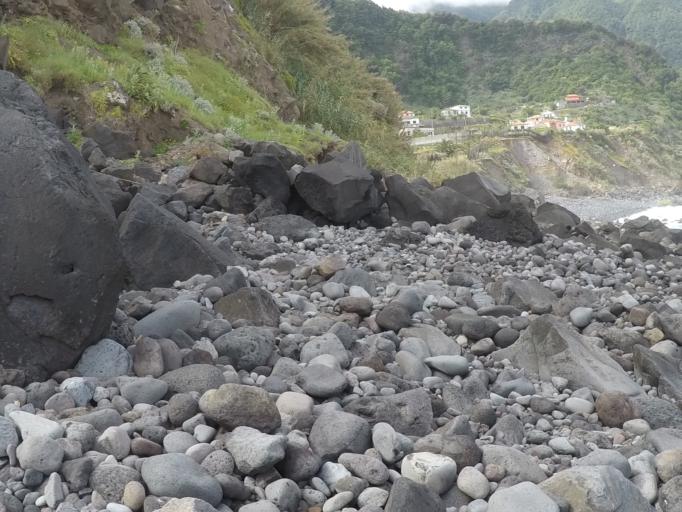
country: PT
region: Madeira
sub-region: Sao Vicente
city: Sao Vicente
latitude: 32.8256
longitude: -16.9970
